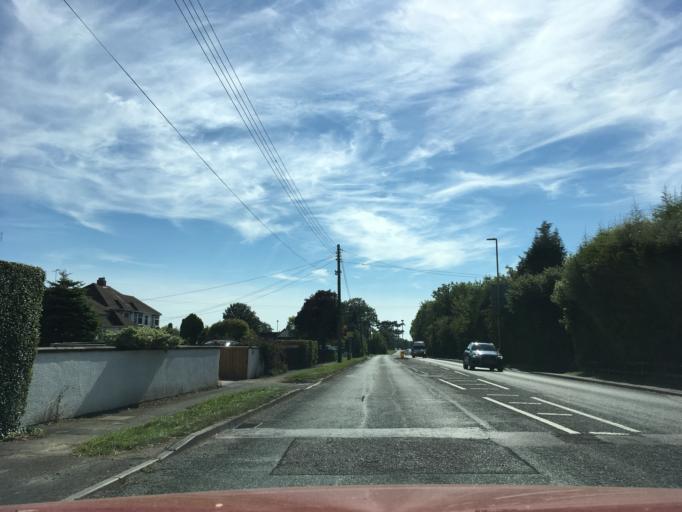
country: GB
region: England
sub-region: South Gloucestershire
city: Alveston
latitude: 51.5759
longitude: -2.5423
